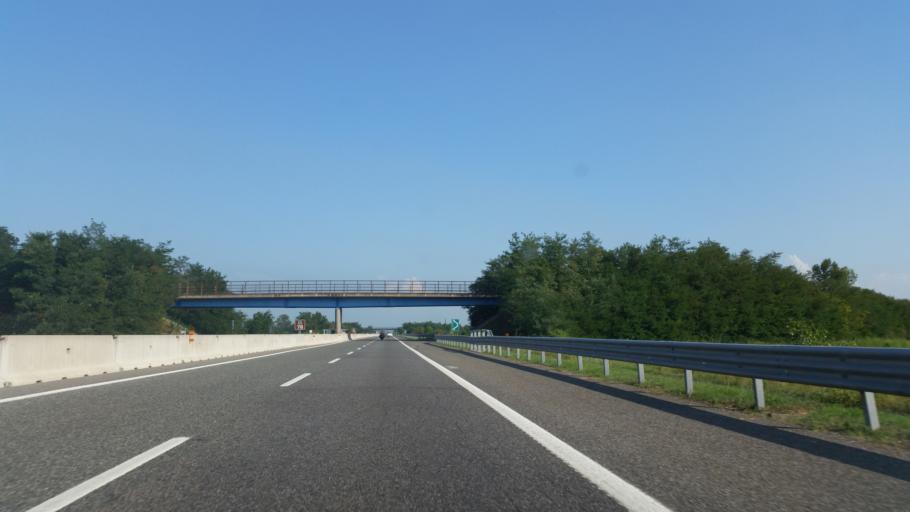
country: IT
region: Piedmont
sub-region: Provincia di Vercelli
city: Asigliano Vercellese
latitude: 45.2834
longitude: 8.4006
